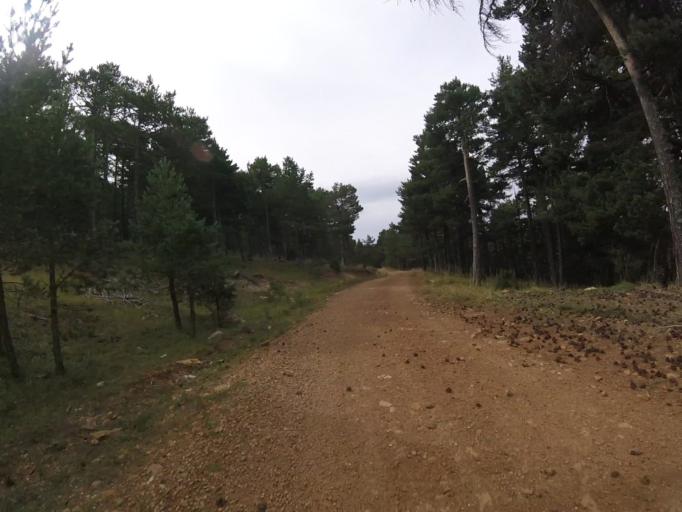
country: ES
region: Aragon
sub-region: Provincia de Teruel
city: Valdelinares
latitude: 40.3550
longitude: -0.5982
